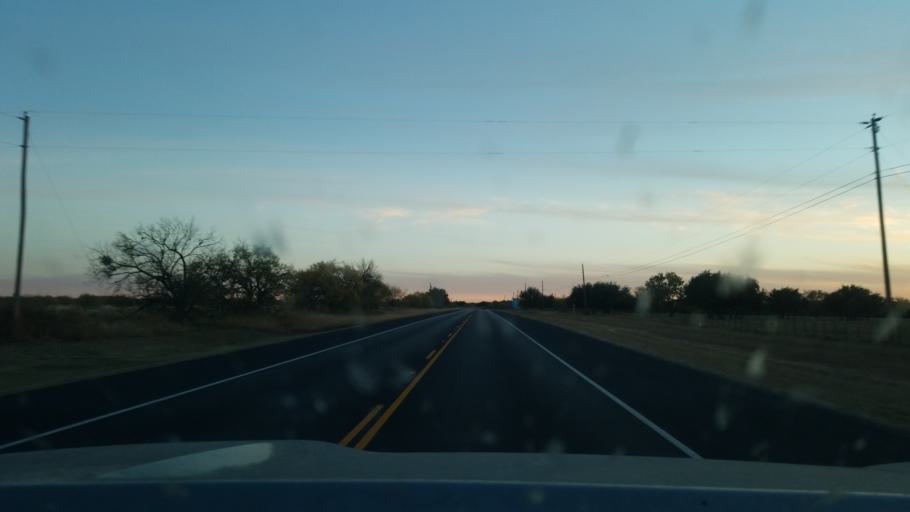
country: US
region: Texas
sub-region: Stephens County
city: Breckenridge
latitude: 32.6306
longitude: -98.9029
